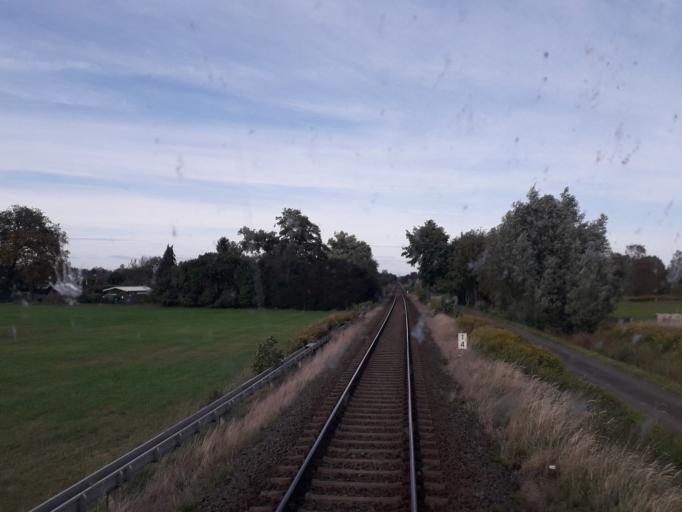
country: DE
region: Brandenburg
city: Kremmen
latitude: 52.7604
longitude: 13.0376
